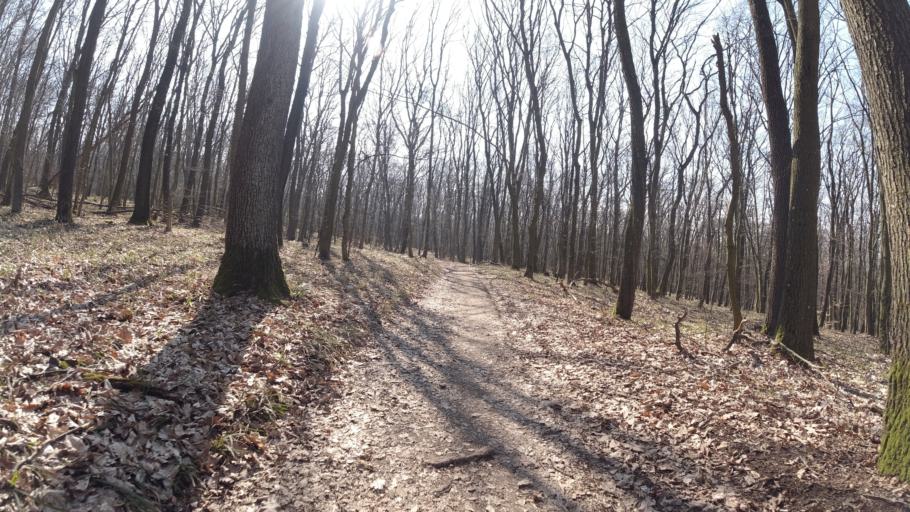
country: SK
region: Trnavsky
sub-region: Okres Trnava
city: Piestany
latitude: 48.5620
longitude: 17.8706
